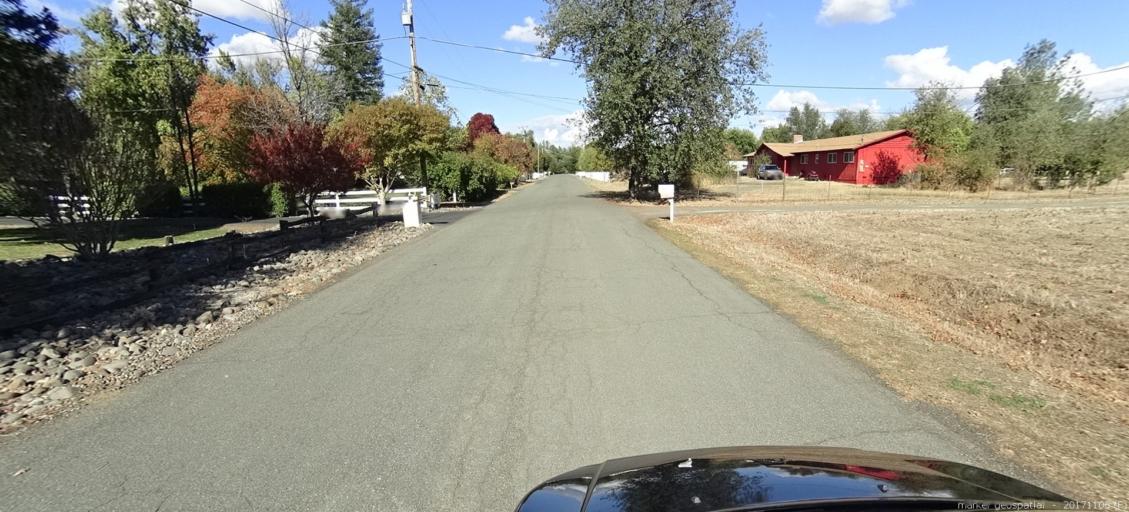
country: US
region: California
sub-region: Shasta County
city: Palo Cedro
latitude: 40.5717
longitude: -122.2237
